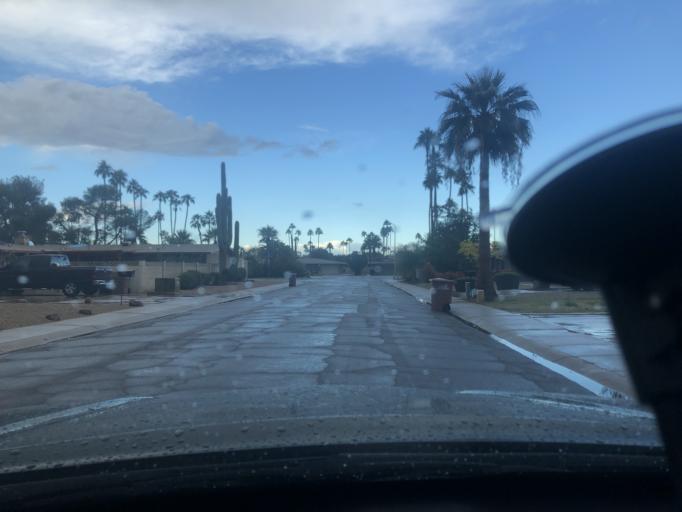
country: US
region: Arizona
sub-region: Maricopa County
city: Scottsdale
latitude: 33.4971
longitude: -111.8924
